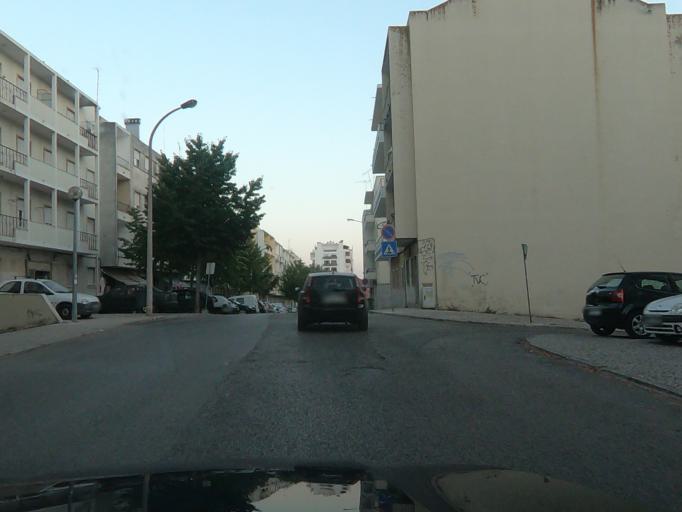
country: PT
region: Setubal
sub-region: Setubal
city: Setubal
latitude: 38.5360
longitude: -8.8949
